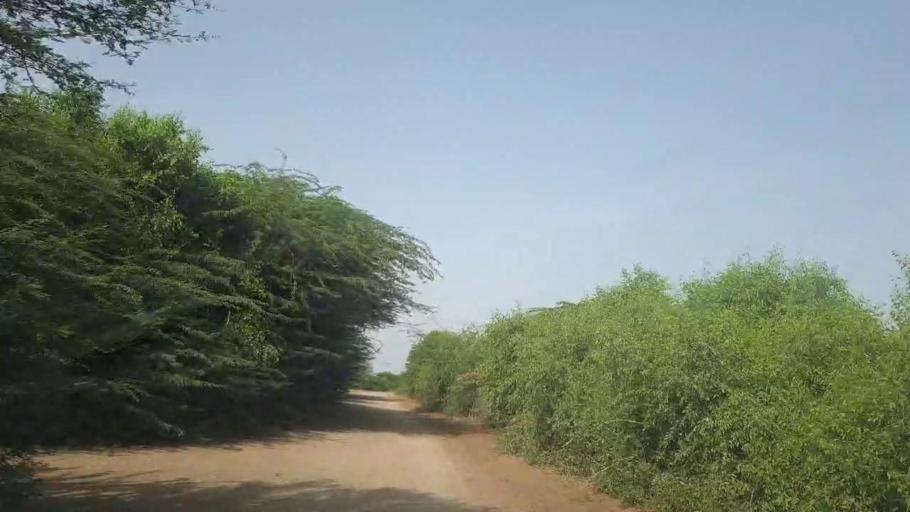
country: PK
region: Sindh
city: Tando Bago
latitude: 24.7912
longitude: 69.1403
